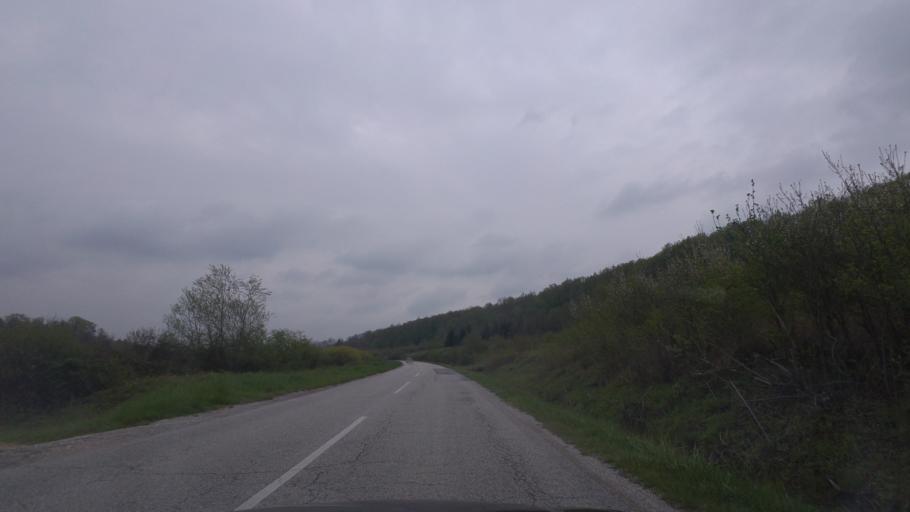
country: HR
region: Karlovacka
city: Ozalj
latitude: 45.6408
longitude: 15.5317
